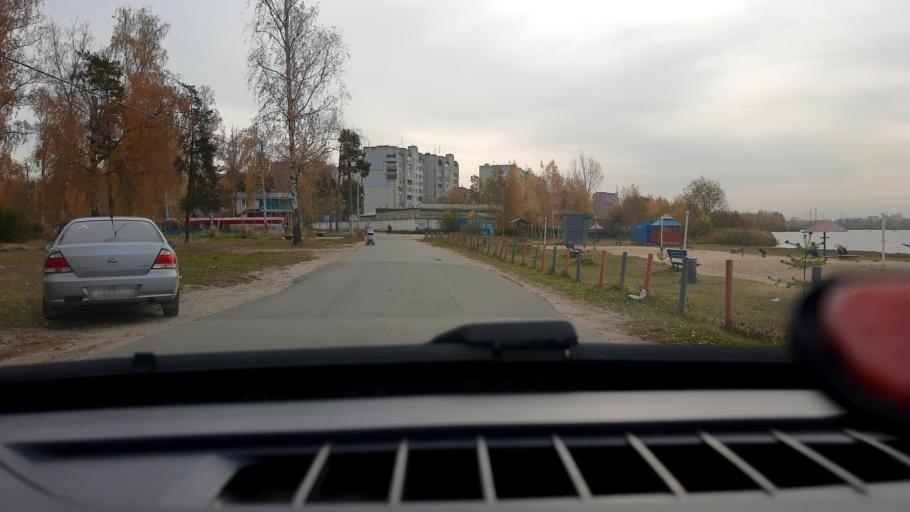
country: RU
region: Nizjnij Novgorod
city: Gorbatovka
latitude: 56.2932
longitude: 43.8364
